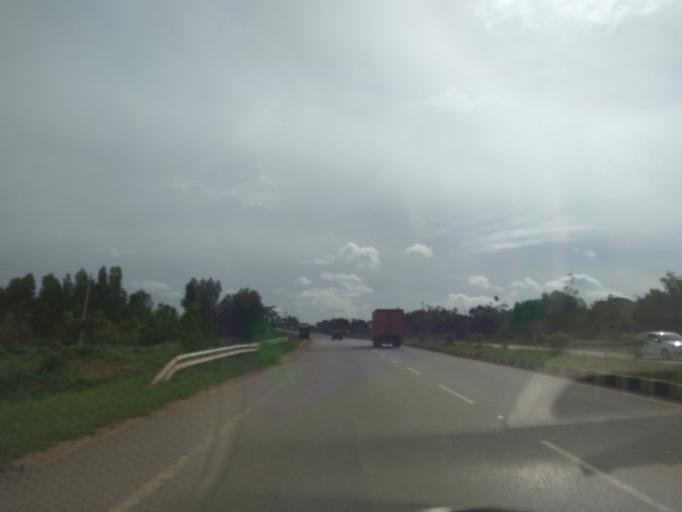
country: IN
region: Karnataka
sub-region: Bangalore Rural
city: Dasarahalli
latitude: 13.0914
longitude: 77.8405
